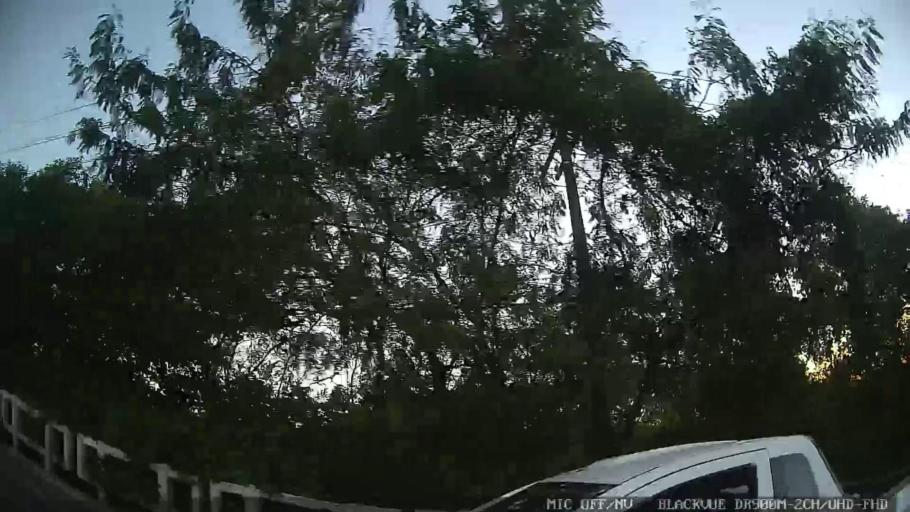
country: BR
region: Sao Paulo
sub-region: Guaruja
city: Guaruja
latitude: -23.9820
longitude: -46.2689
